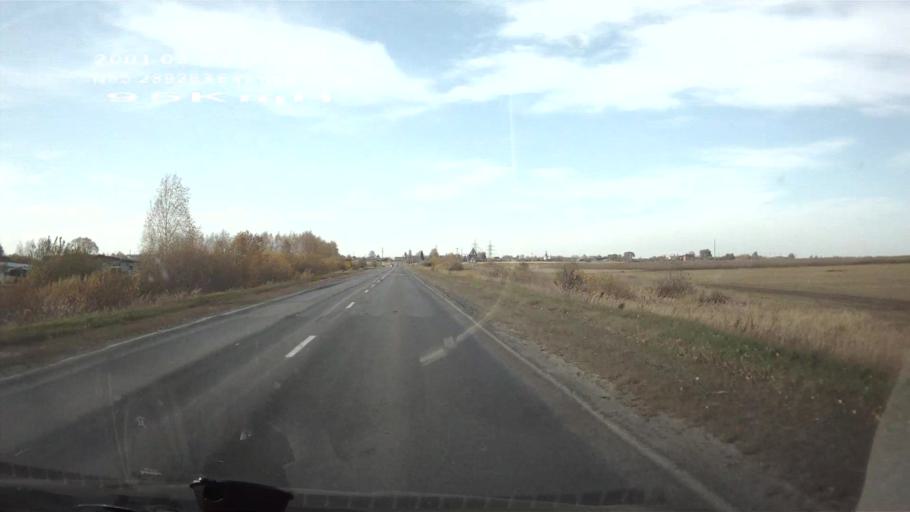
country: RU
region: Chuvashia
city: Ibresi
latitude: 55.2892
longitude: 47.0664
